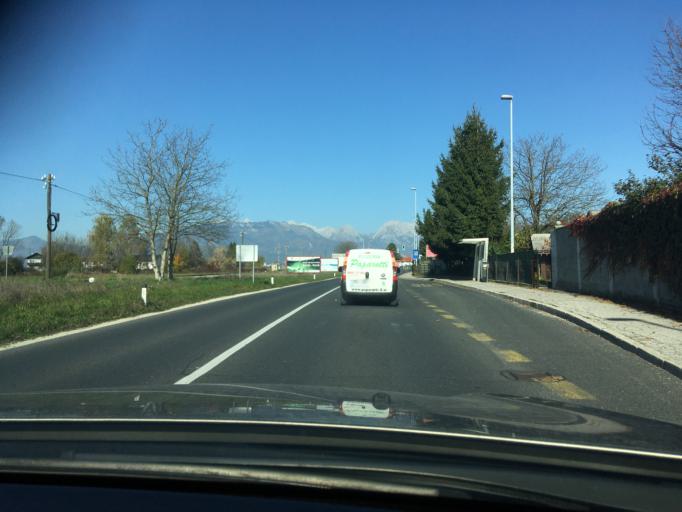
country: SI
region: Domzale
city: Domzale
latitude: 46.1493
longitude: 14.5927
